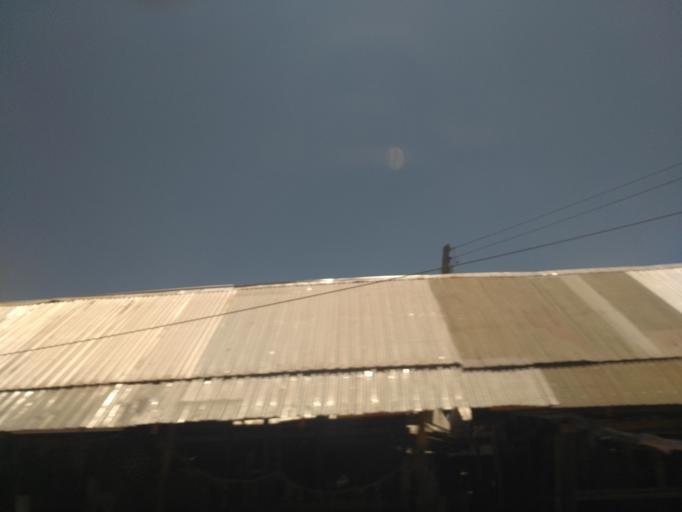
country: TZ
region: Dodoma
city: Dodoma
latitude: -6.1651
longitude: 35.7421
